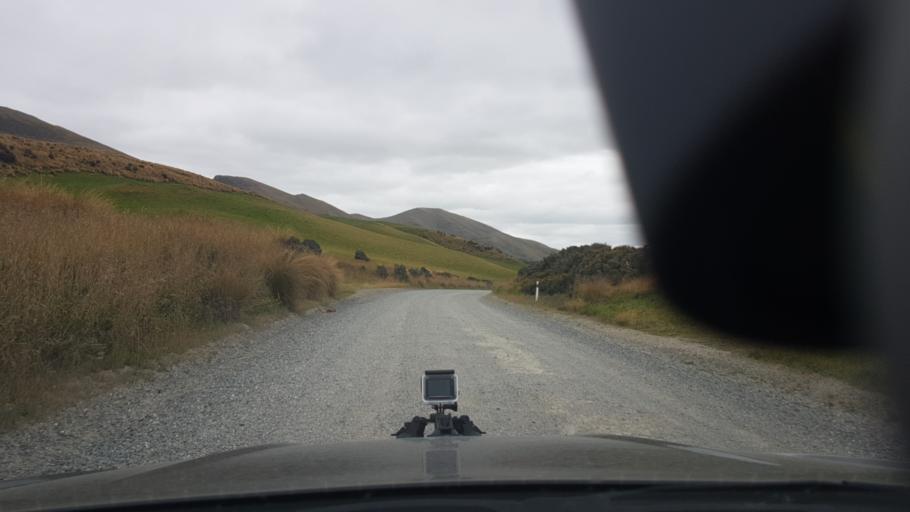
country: NZ
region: Otago
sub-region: Clutha District
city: Papatowai
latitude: -46.3258
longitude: 169.3853
